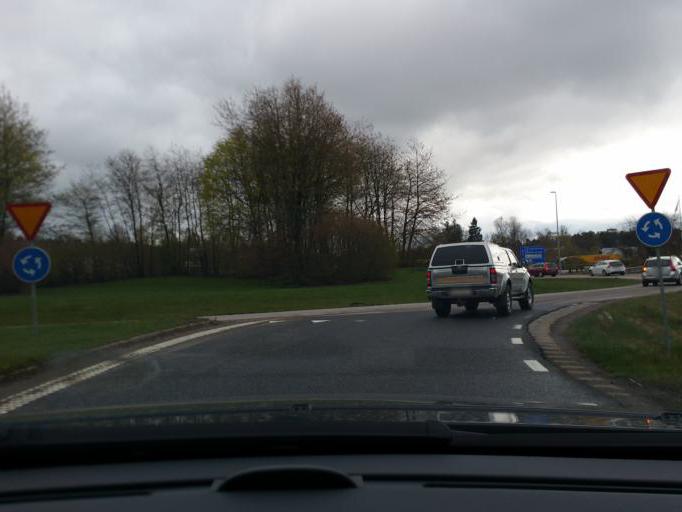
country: SE
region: Kronoberg
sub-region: Vaxjo Kommun
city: Vaexjoe
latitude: 56.8809
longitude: 14.8328
